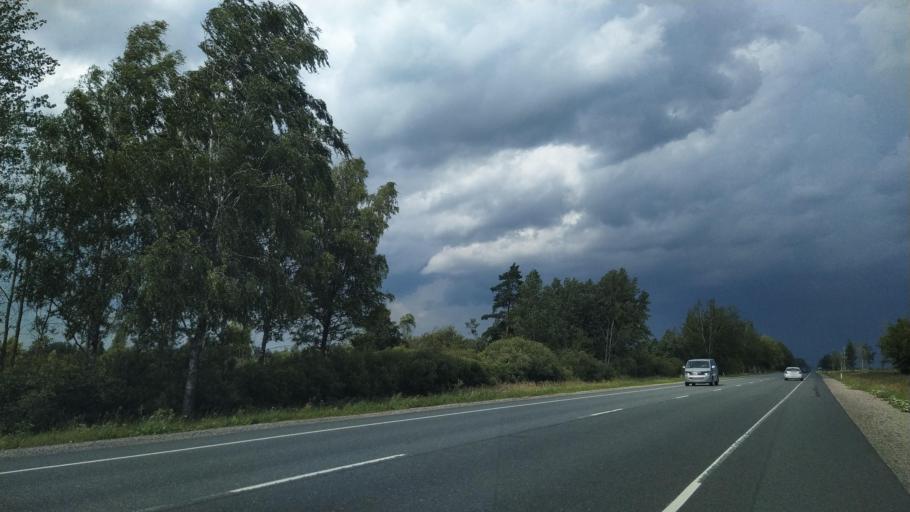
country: RU
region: Pskov
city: Ostrov
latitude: 57.5210
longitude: 28.3322
